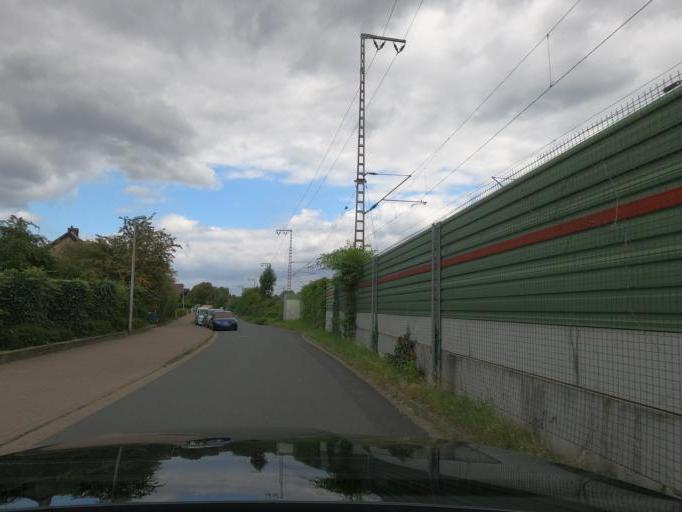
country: DE
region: Lower Saxony
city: Lehrte
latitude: 52.3816
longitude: 9.9688
